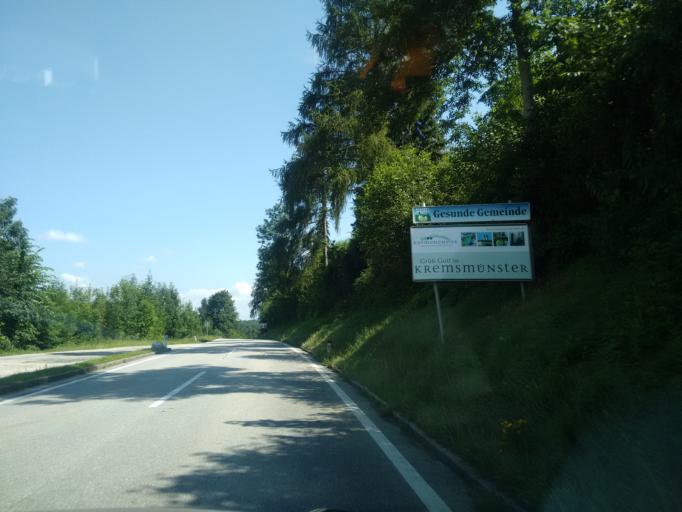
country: AT
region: Upper Austria
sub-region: Politischer Bezirk Kirchdorf an der Krems
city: Kremsmunster
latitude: 48.0455
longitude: 14.1293
